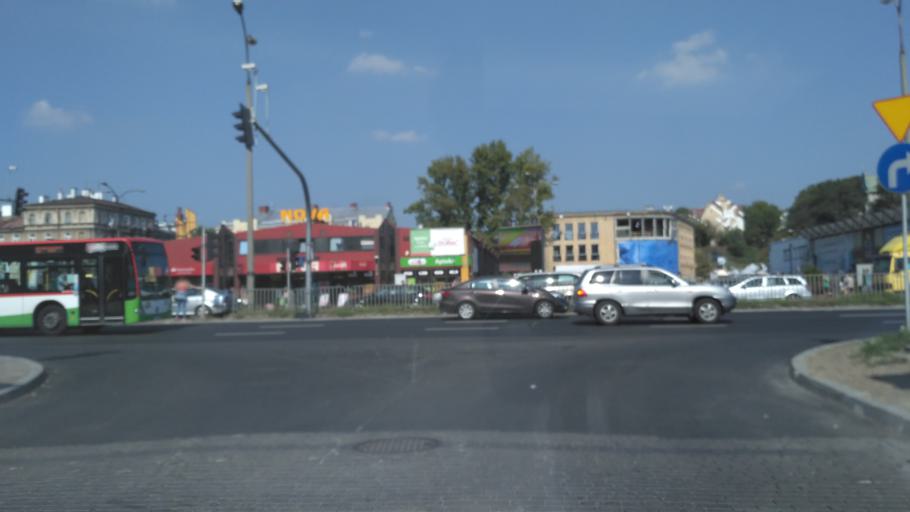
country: PL
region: Lublin Voivodeship
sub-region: Powiat lubelski
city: Lublin
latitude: 51.2513
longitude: 22.5703
